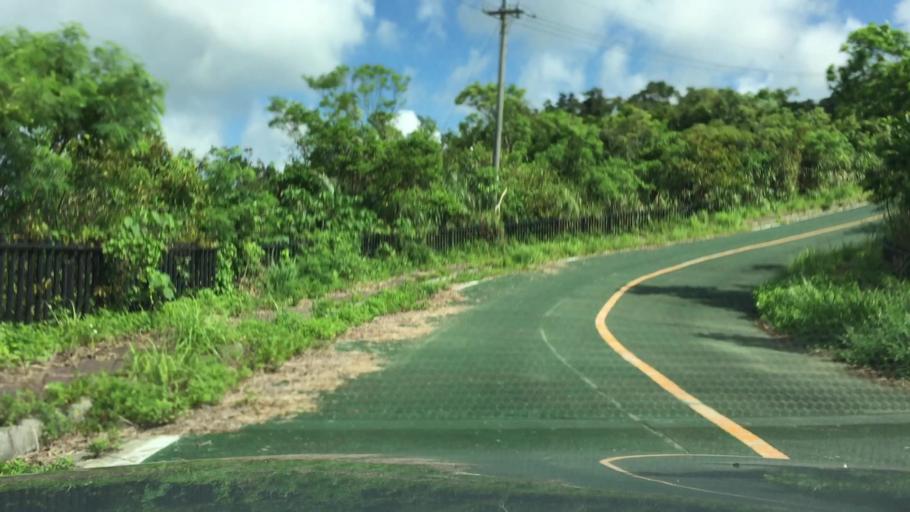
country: JP
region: Okinawa
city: Ishigaki
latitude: 24.3770
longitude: 124.1642
